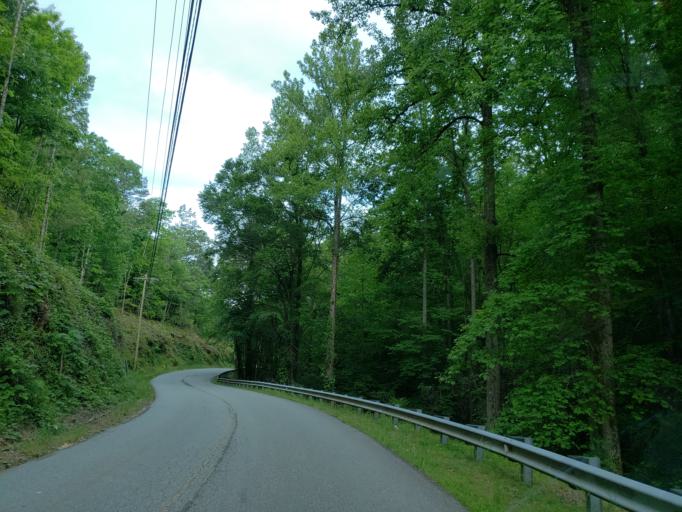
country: US
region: Georgia
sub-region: Fannin County
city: Blue Ridge
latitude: 34.8567
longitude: -84.3386
